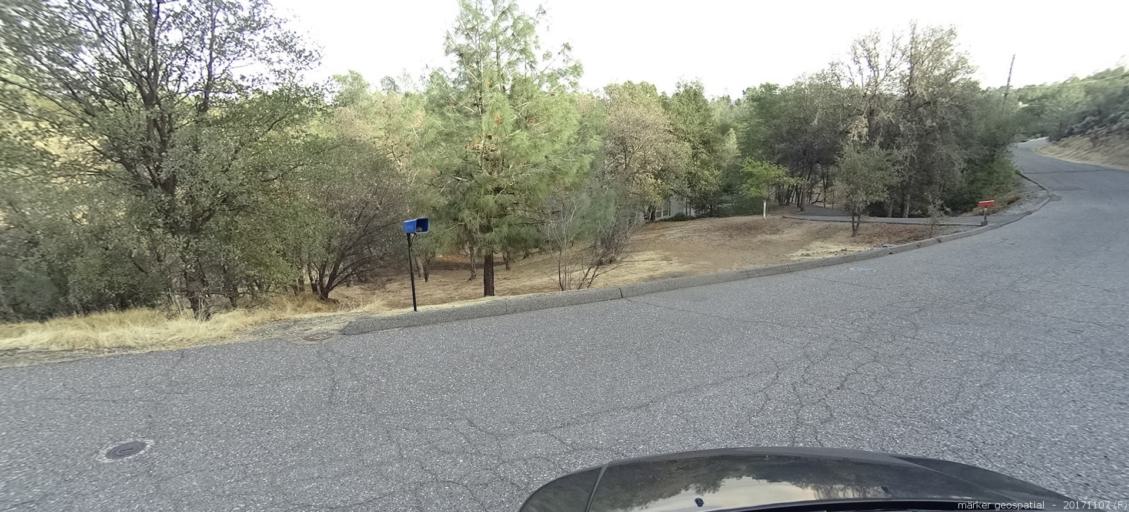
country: US
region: California
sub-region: Shasta County
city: Shasta
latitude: 40.5310
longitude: -122.4869
